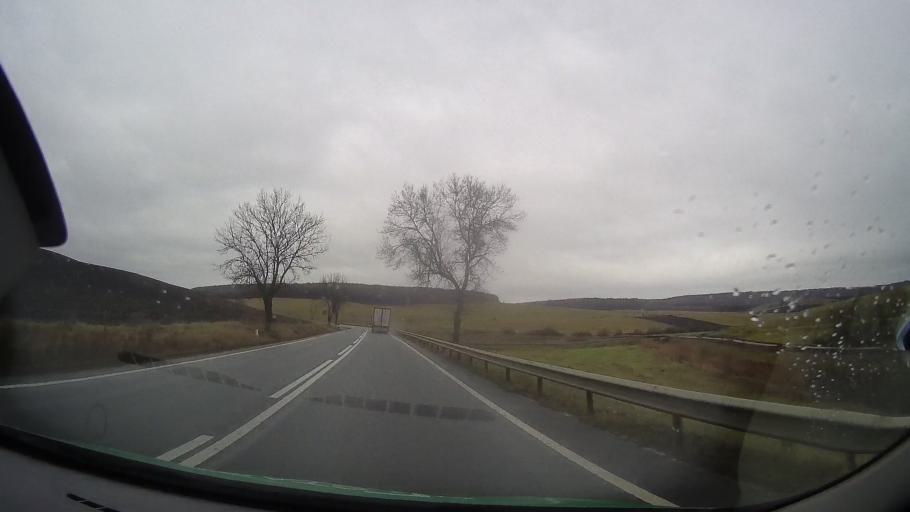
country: RO
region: Mures
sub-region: Comuna Lunca
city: Lunca
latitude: 46.8639
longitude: 24.5541
